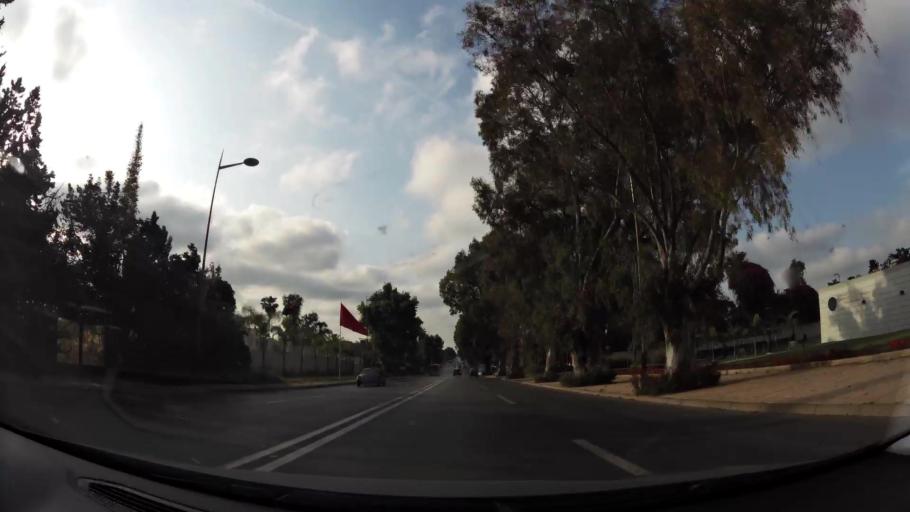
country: MA
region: Rabat-Sale-Zemmour-Zaer
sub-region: Rabat
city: Rabat
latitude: 33.9561
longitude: -6.8252
